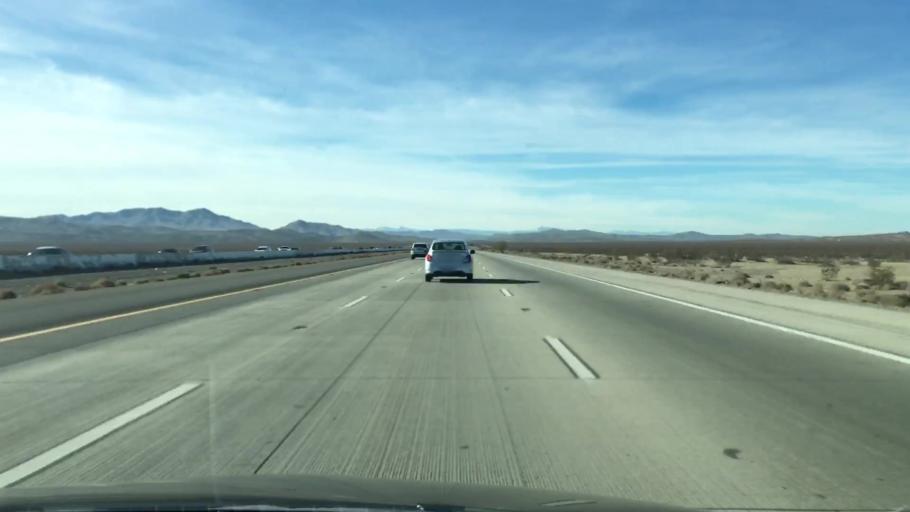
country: US
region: California
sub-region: San Bernardino County
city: Lenwood
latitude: 34.7983
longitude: -117.1107
